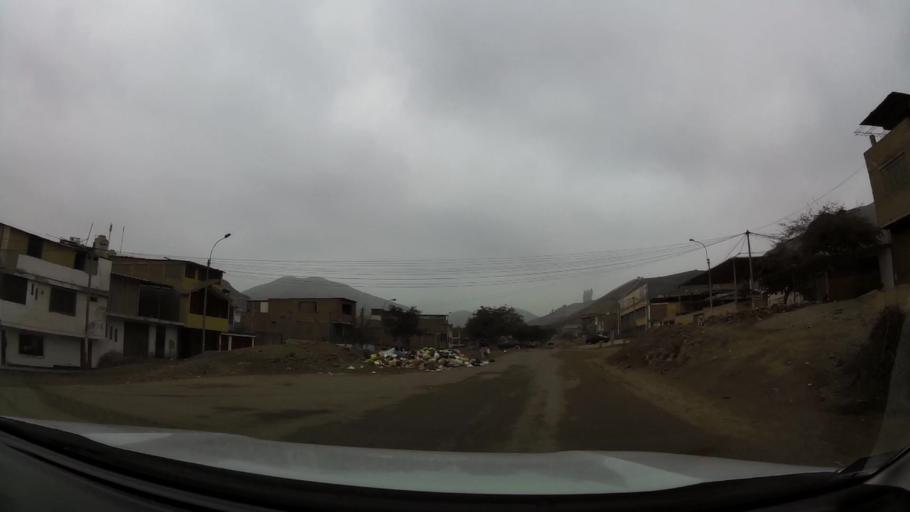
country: PE
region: Lima
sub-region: Lima
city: Cieneguilla
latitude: -12.2092
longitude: -76.9037
